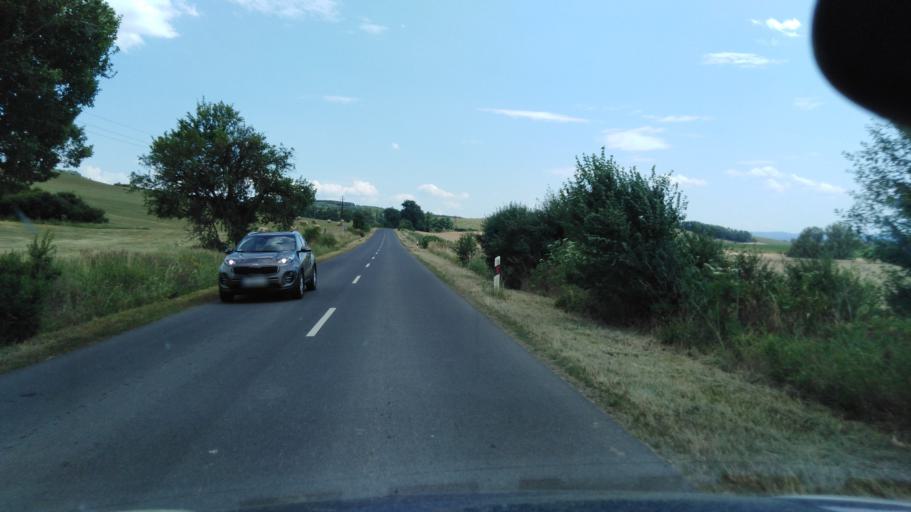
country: HU
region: Nograd
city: Szecseny
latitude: 48.1690
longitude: 19.5344
